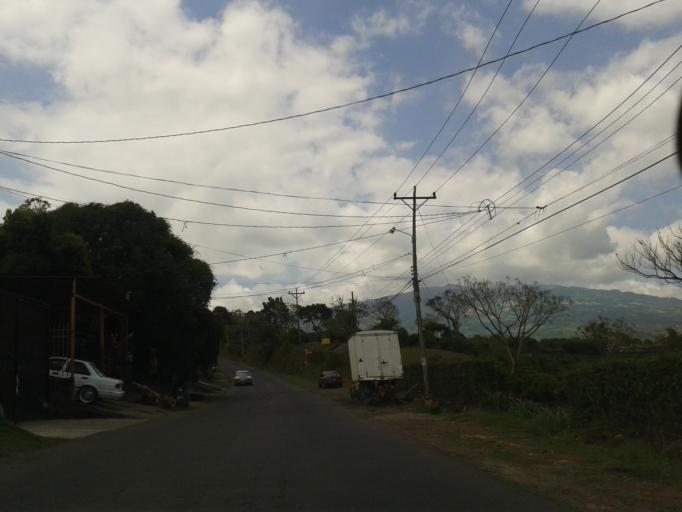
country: CR
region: Alajuela
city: Sabanilla
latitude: 10.0610
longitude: -84.1982
